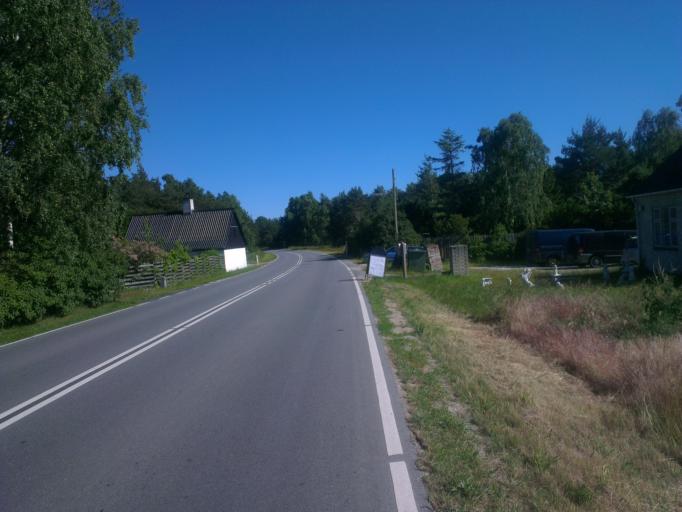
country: DK
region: Capital Region
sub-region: Frederikssund Kommune
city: Jaegerspris
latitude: 55.8985
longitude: 11.9466
